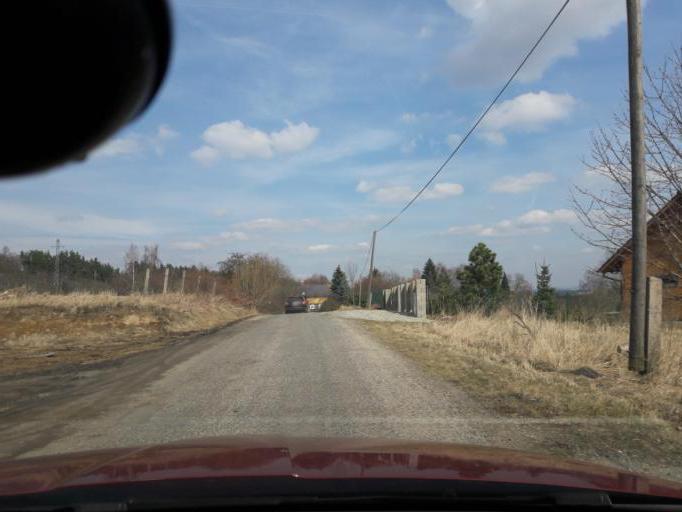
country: CZ
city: Zakupy
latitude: 50.7183
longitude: 14.6118
